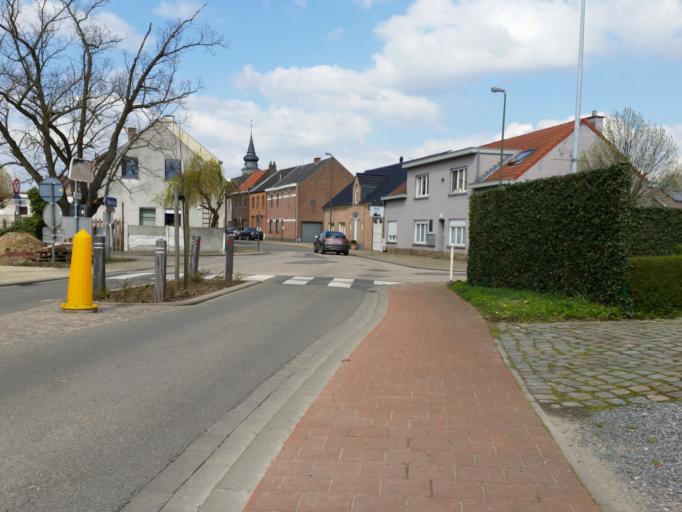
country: BE
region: Flanders
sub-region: Provincie Vlaams-Brabant
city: Haacht
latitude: 50.9355
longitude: 4.6170
